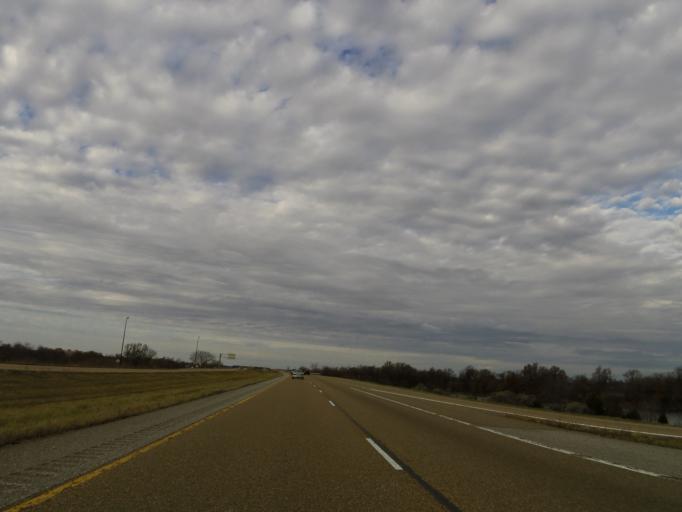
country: US
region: Illinois
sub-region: Clinton County
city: Wamac
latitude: 38.3898
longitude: -89.1721
